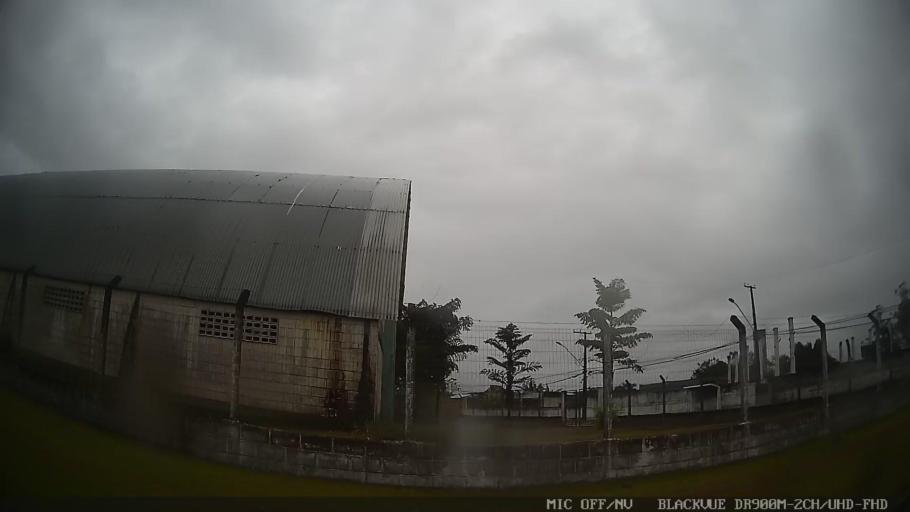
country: BR
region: Sao Paulo
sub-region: Itanhaem
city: Itanhaem
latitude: -24.1763
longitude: -46.8280
